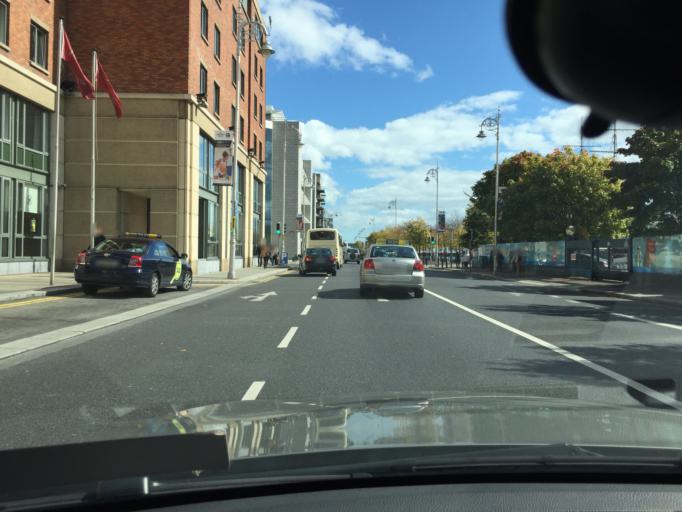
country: IE
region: Leinster
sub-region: Dublin City
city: Dublin
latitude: 53.3481
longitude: -6.2469
